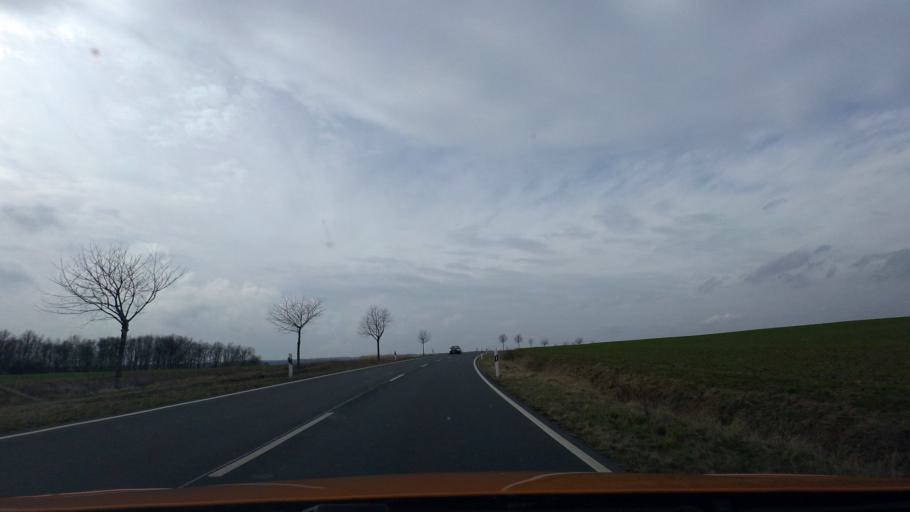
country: DE
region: Lower Saxony
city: Supplingen
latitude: 52.2267
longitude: 10.8827
